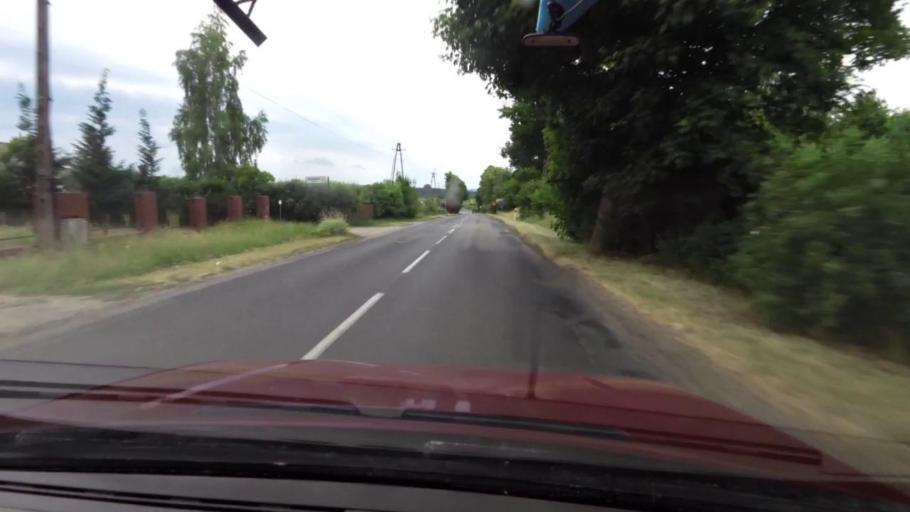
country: PL
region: West Pomeranian Voivodeship
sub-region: Powiat koszalinski
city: Sianow
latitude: 54.1720
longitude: 16.4013
